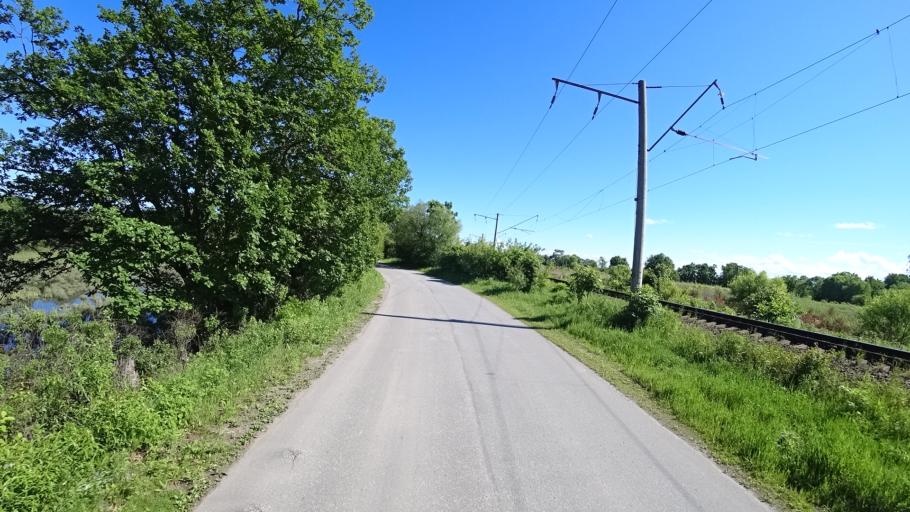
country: RU
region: Khabarovsk Krai
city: Khor
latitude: 47.8902
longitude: 135.0233
